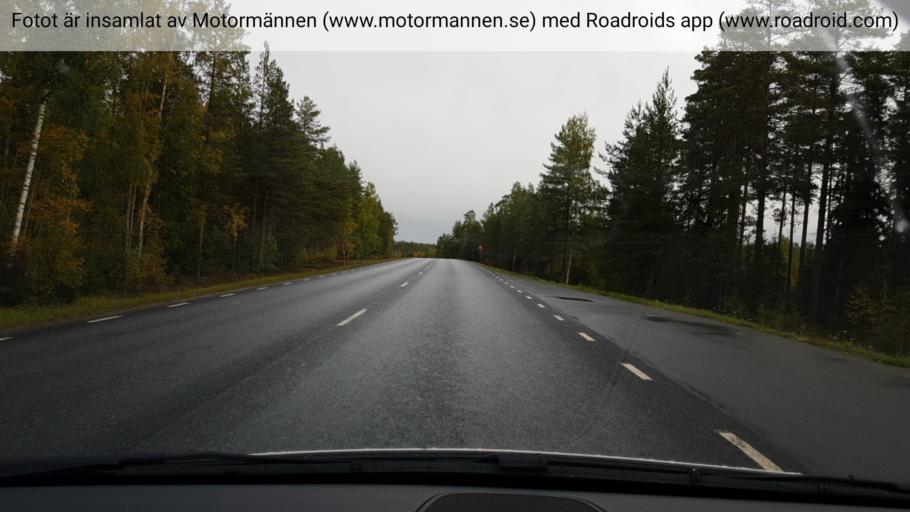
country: SE
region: Vaesterbotten
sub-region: Umea Kommun
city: Ersmark
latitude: 63.8946
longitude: 20.3135
